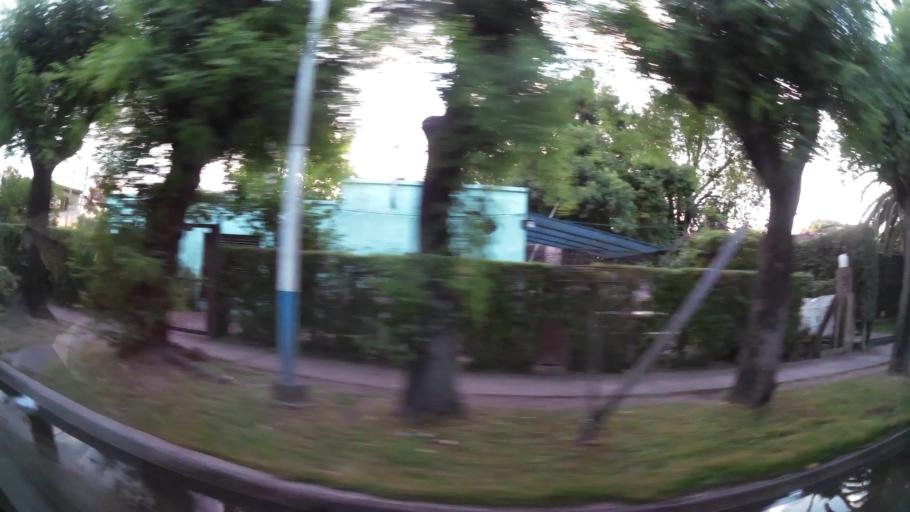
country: AR
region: Buenos Aires
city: Santa Catalina - Dique Lujan
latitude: -34.4754
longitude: -58.7574
